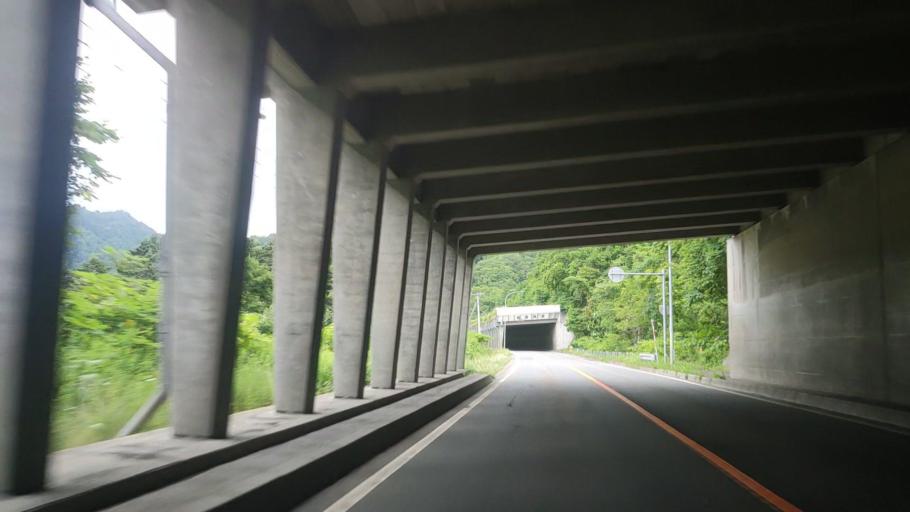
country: JP
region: Hokkaido
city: Niseko Town
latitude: 42.6019
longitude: 140.5711
